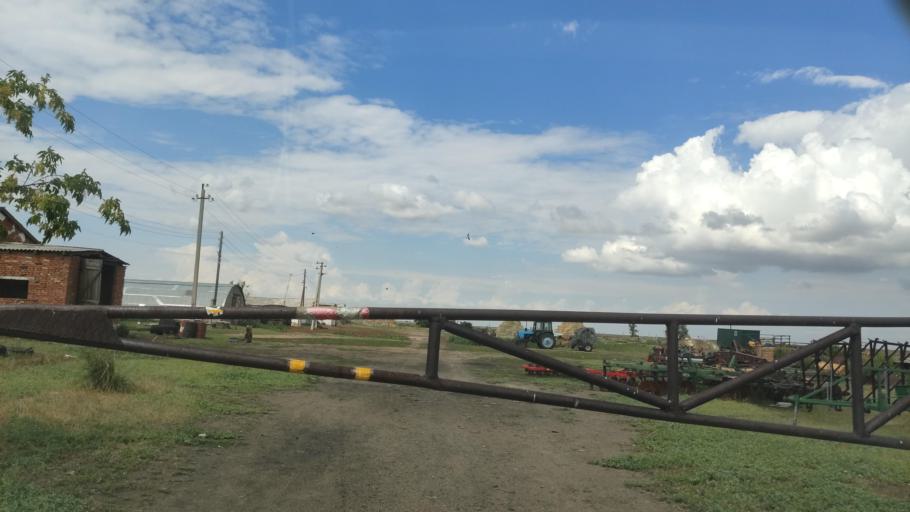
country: KZ
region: Pavlodar
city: Pavlodar
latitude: 52.6511
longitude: 77.0216
